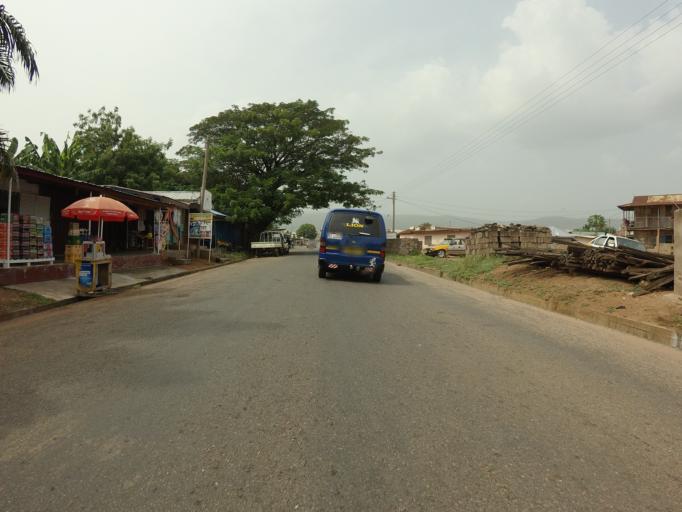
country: GH
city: Akropong
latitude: 6.1033
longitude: -0.0096
